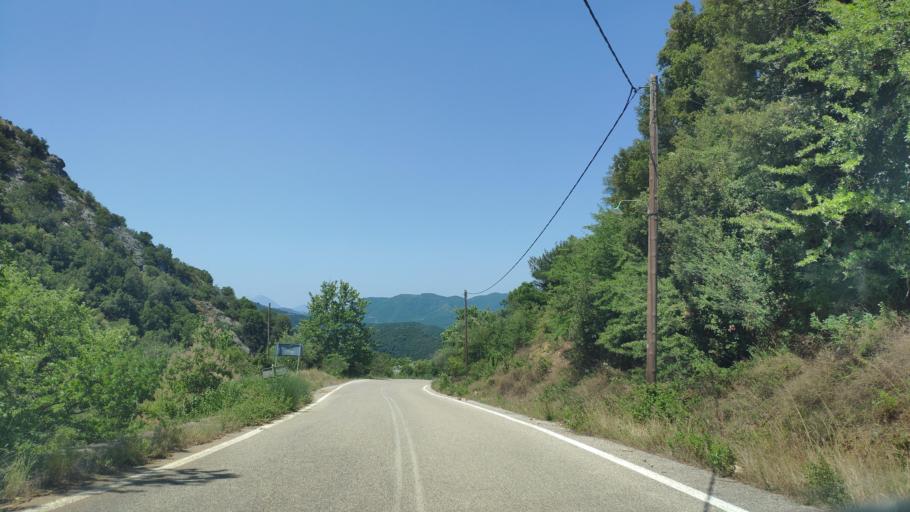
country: GR
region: West Greece
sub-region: Nomos Aitolias kai Akarnanias
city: Sardinia
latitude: 38.9279
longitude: 21.4084
